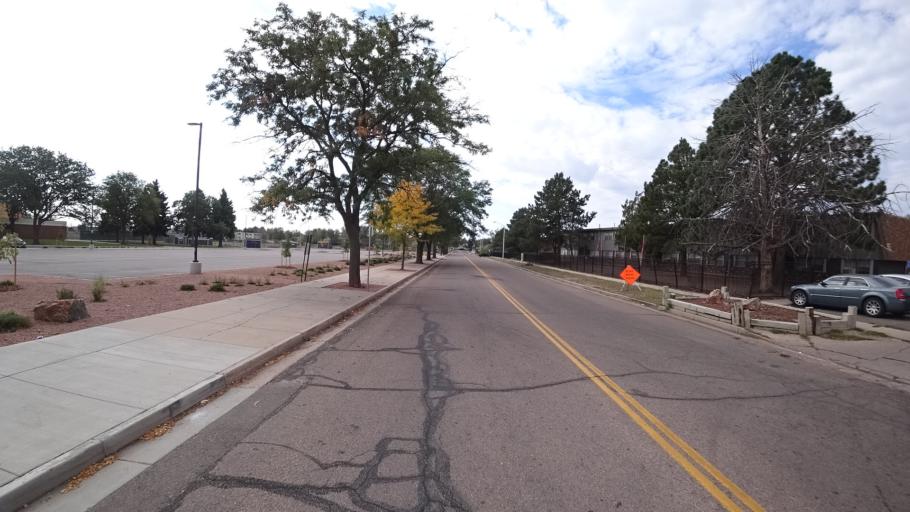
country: US
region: Colorado
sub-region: El Paso County
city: Cimarron Hills
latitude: 38.8492
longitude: -104.7527
